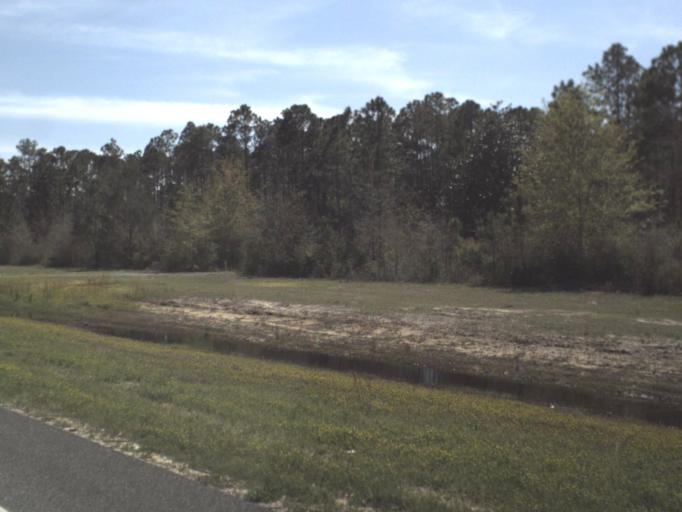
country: US
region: Florida
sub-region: Bay County
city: Lynn Haven
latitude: 30.3703
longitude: -85.6752
